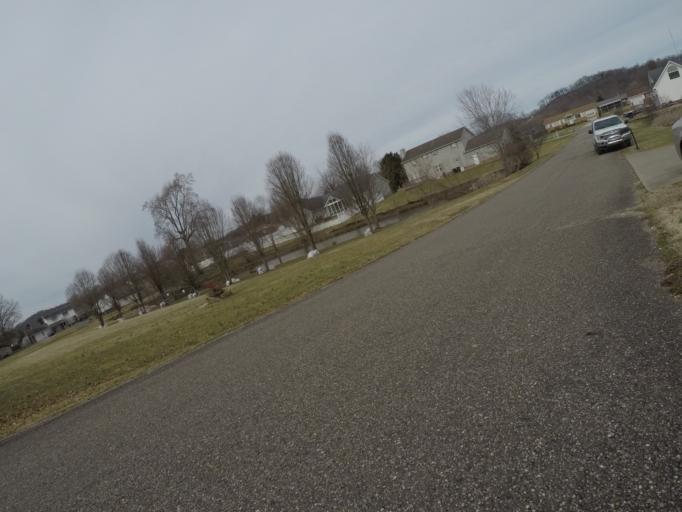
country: US
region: West Virginia
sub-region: Cabell County
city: Pea Ridge
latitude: 38.4499
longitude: -82.3407
